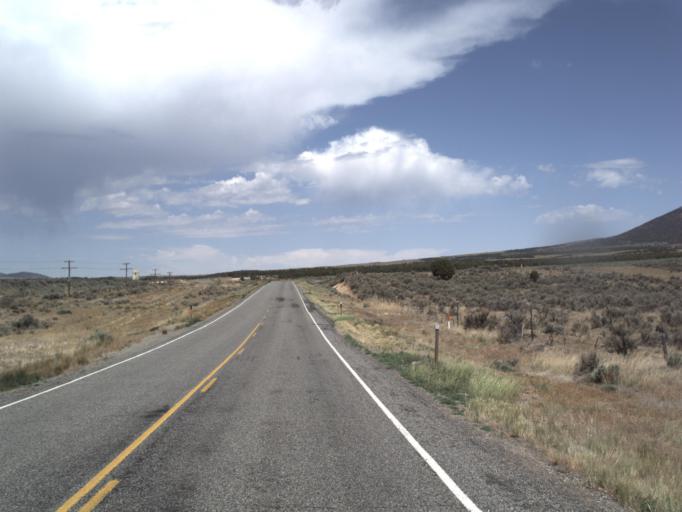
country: US
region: Utah
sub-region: Utah County
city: Genola
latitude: 39.9355
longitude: -112.1763
